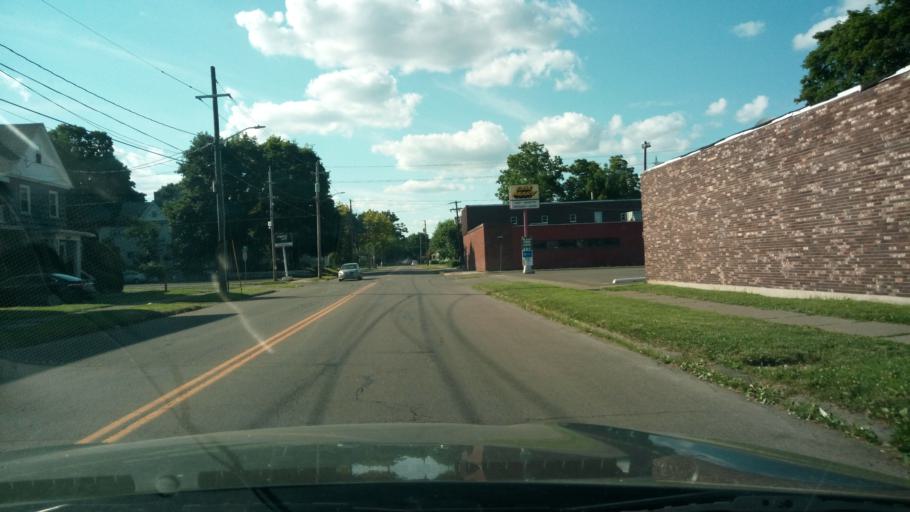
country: US
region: New York
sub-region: Chemung County
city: Elmira
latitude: 42.0895
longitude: -76.8188
